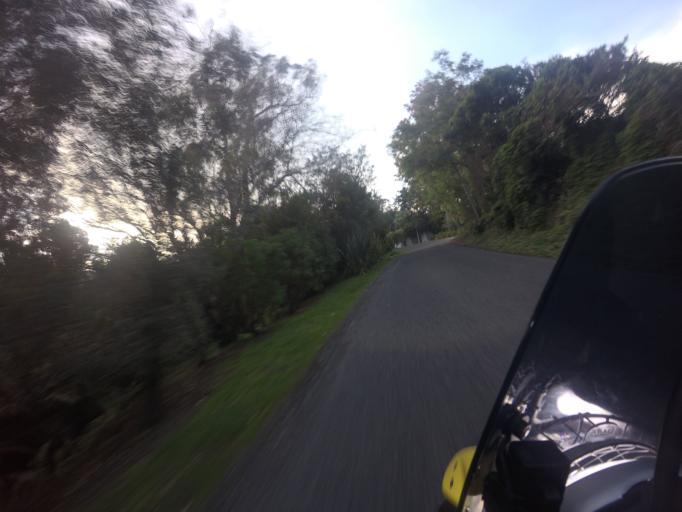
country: NZ
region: Gisborne
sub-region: Gisborne District
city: Gisborne
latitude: -38.6658
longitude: 178.0530
